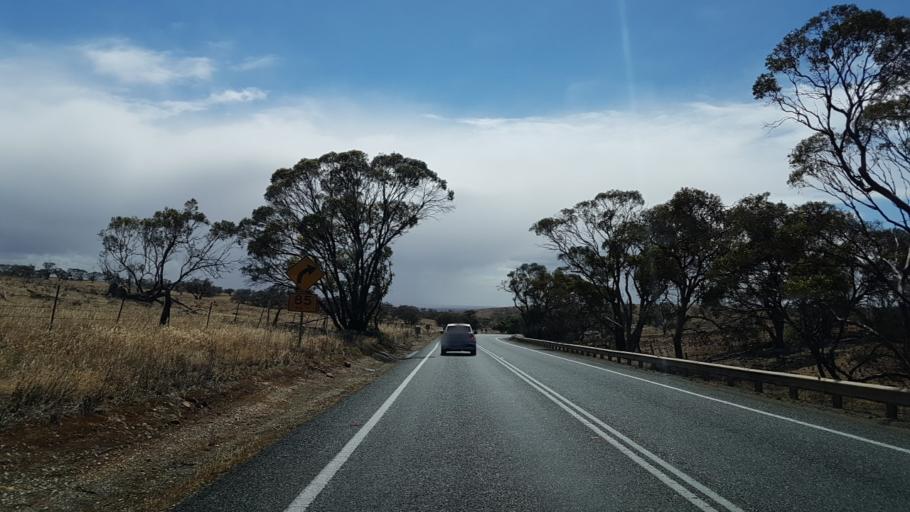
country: AU
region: South Australia
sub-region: Barossa
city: Angaston
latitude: -34.3990
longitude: 139.2005
